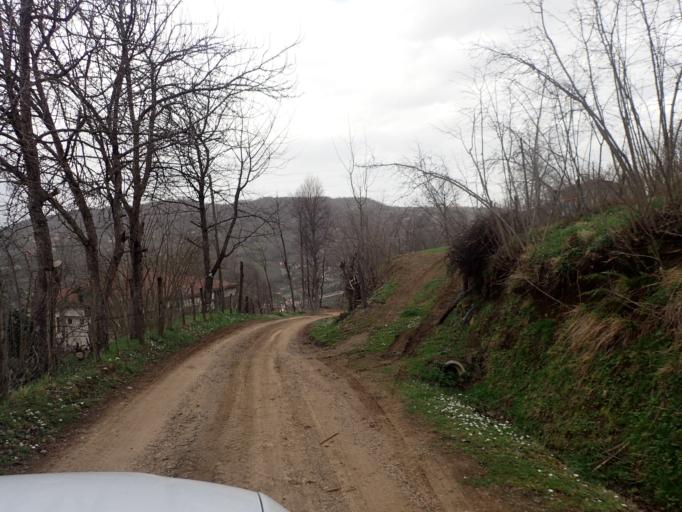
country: TR
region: Ordu
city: Camas
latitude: 40.8917
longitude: 37.4973
